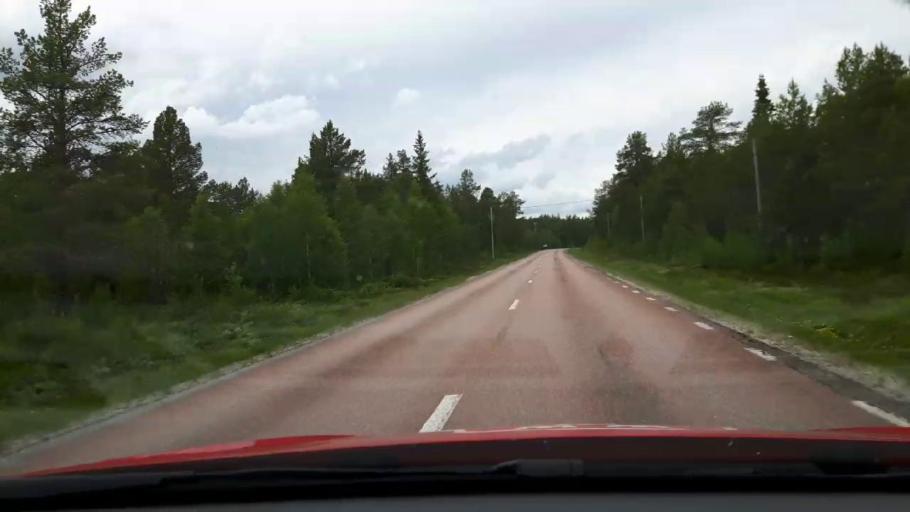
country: NO
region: Hedmark
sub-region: Engerdal
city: Engerdal
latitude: 62.4915
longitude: 12.6409
